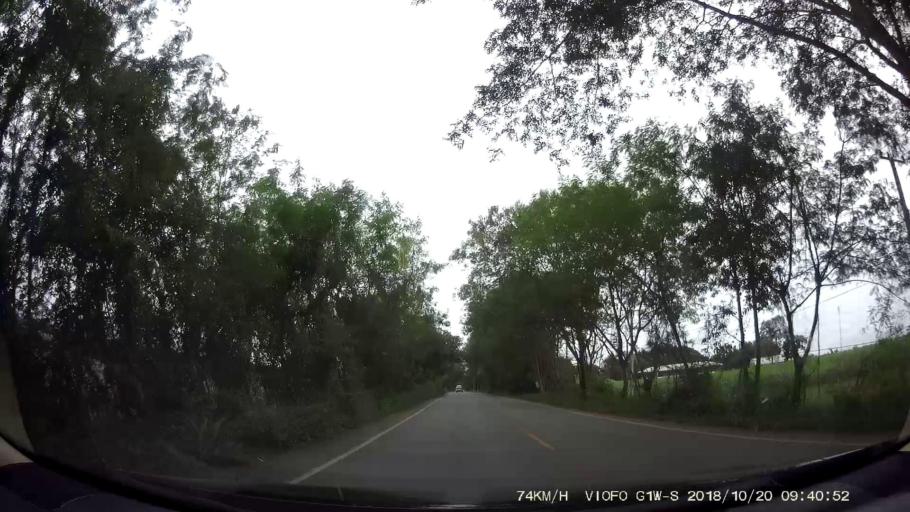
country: TH
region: Chaiyaphum
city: Kaset Sombun
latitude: 16.4473
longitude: 101.9596
